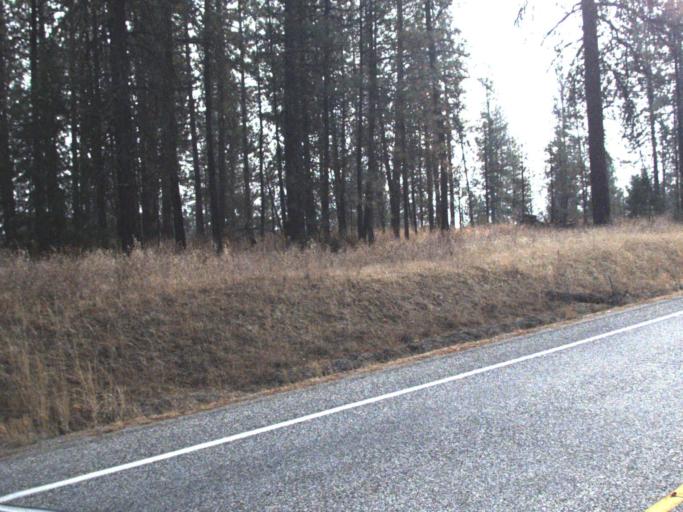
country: US
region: Washington
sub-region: Stevens County
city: Kettle Falls
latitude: 48.7694
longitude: -118.1412
